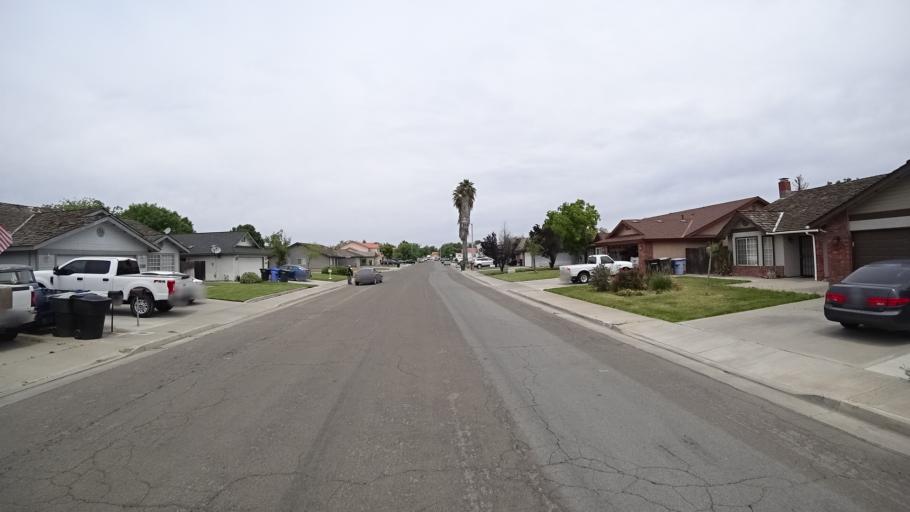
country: US
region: California
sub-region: Kings County
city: Hanford
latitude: 36.3547
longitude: -119.6286
